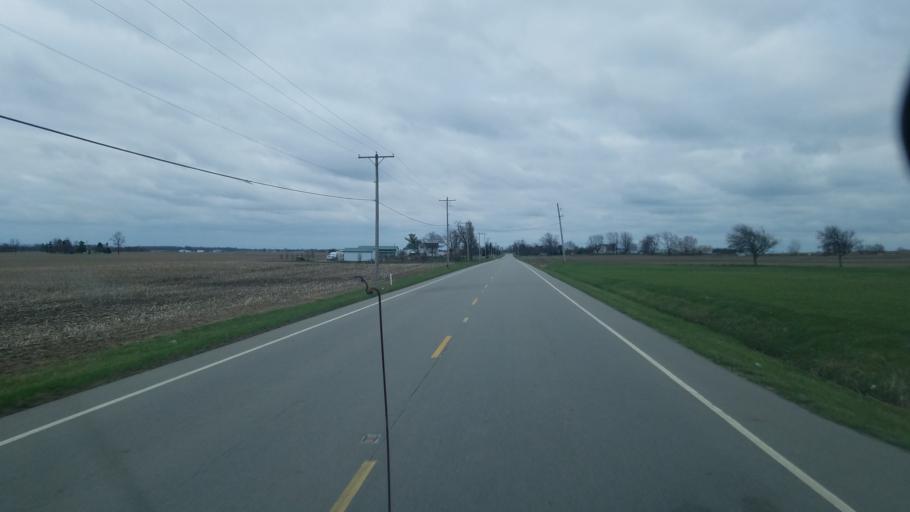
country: US
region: Ohio
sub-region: Fayette County
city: Washington Court House
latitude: 39.5627
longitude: -83.4999
